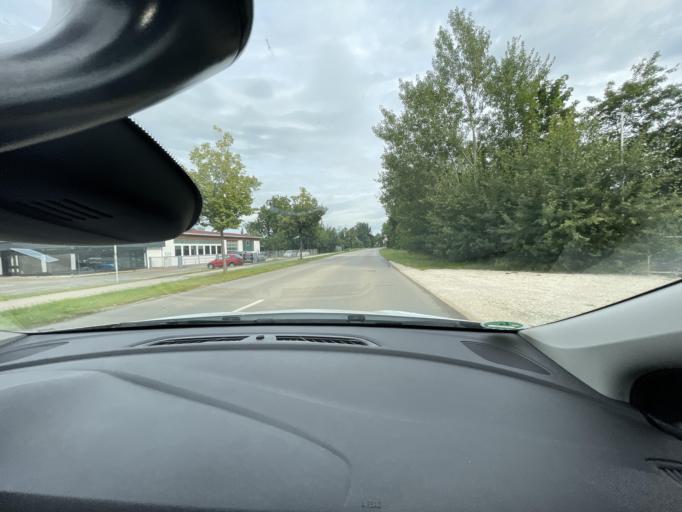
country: DE
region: Bavaria
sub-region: Swabia
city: Langweid
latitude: 48.4684
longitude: 10.8657
